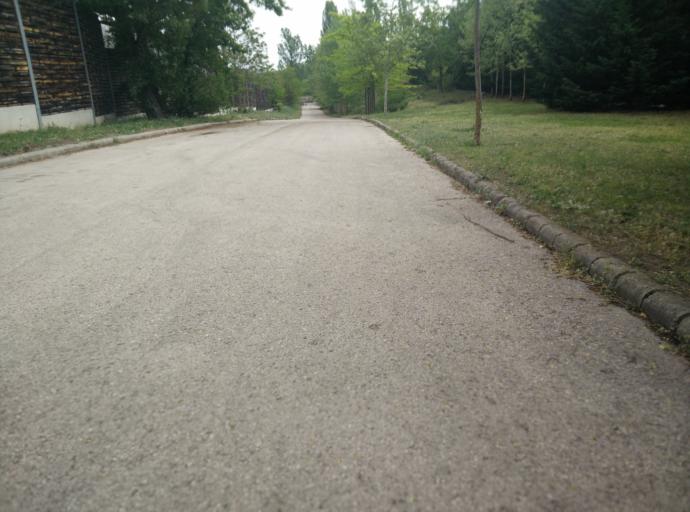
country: HU
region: Pest
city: Dunakeszi
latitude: 47.6065
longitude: 19.1051
